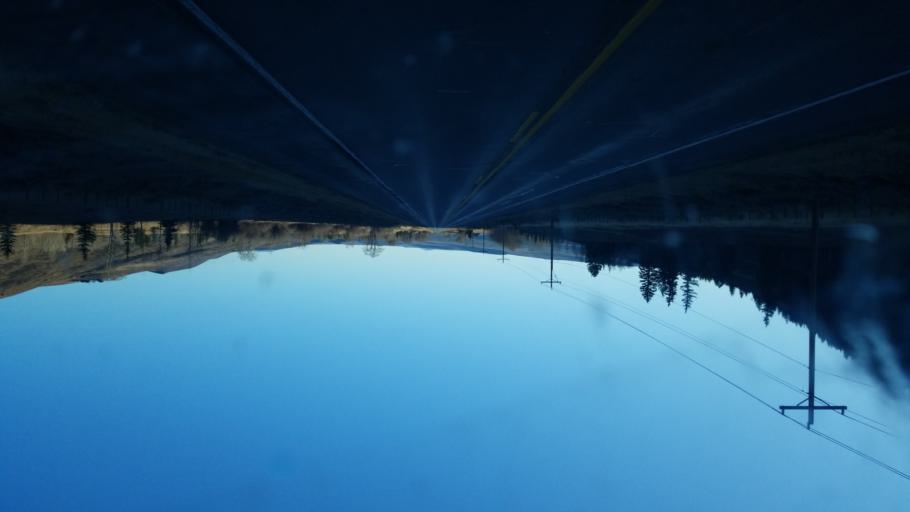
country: US
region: Colorado
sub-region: Gunnison County
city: Crested Butte
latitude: 38.7781
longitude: -106.8692
